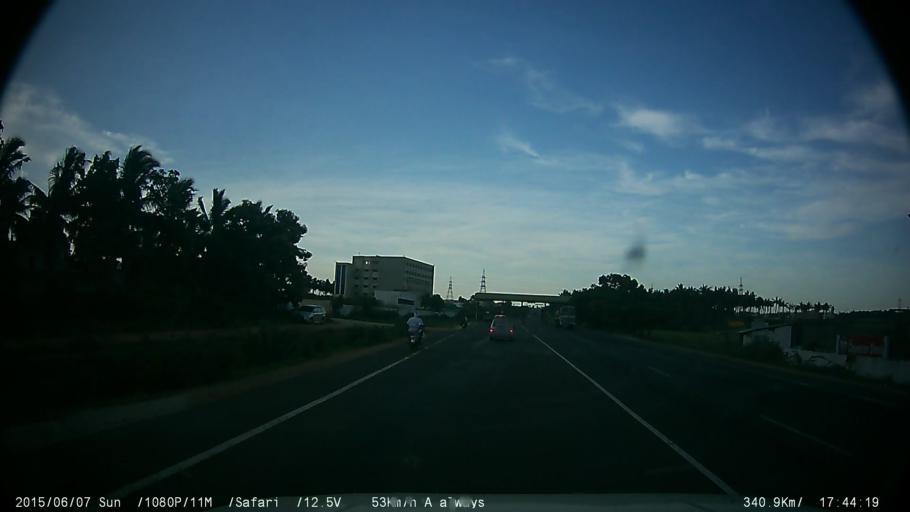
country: IN
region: Tamil Nadu
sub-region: Coimbatore
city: Madukkarai
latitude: 10.9136
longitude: 76.9817
